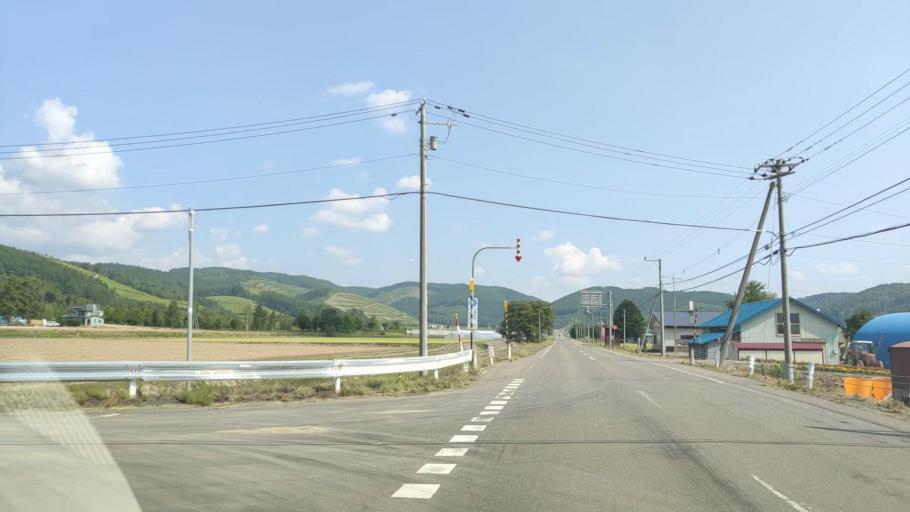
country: JP
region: Hokkaido
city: Shimo-furano
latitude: 43.4060
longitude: 142.3958
